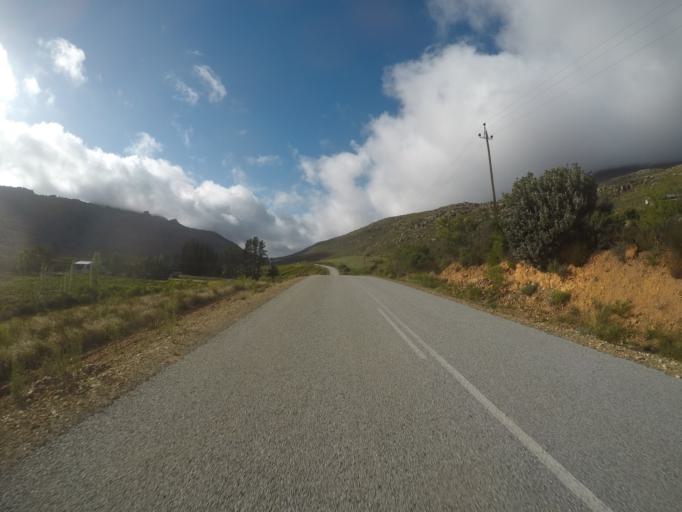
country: ZA
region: Western Cape
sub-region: West Coast District Municipality
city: Clanwilliam
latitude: -32.3617
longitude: 18.8554
